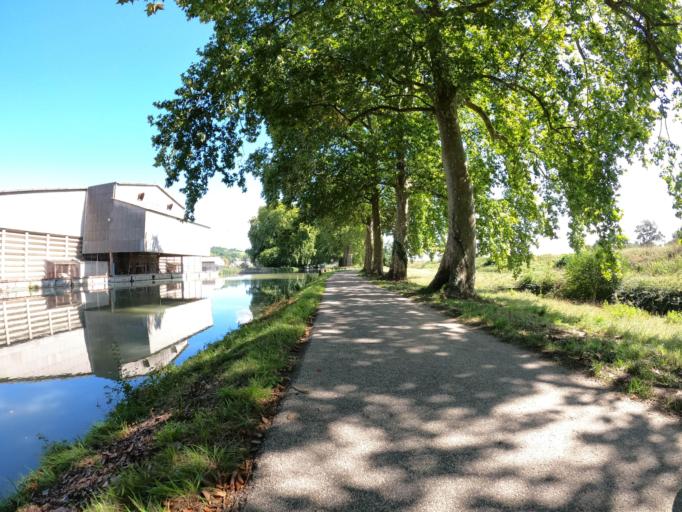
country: FR
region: Midi-Pyrenees
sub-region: Departement du Tarn-et-Garonne
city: Saint-Nicolas-de-la-Grave
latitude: 44.0899
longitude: 0.9634
